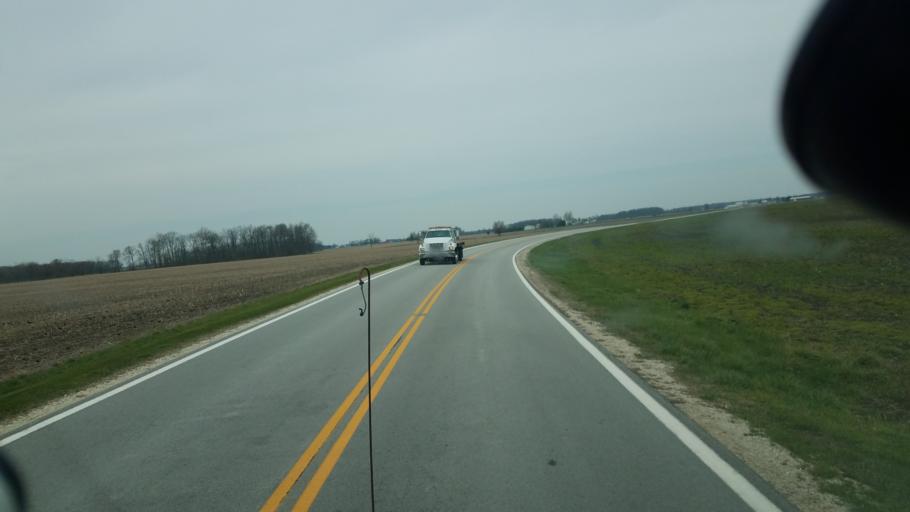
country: US
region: Ohio
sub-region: Wyandot County
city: Carey
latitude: 40.9920
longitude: -83.4772
